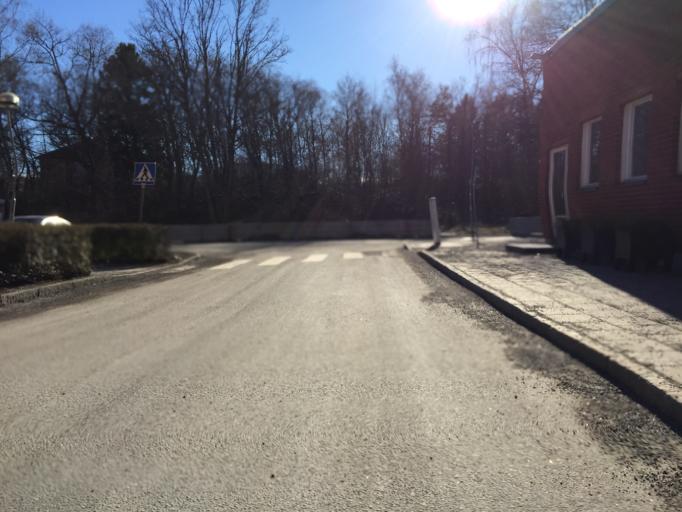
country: SE
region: Stockholm
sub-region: Stockholms Kommun
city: Bromma
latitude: 59.3584
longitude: 17.9008
